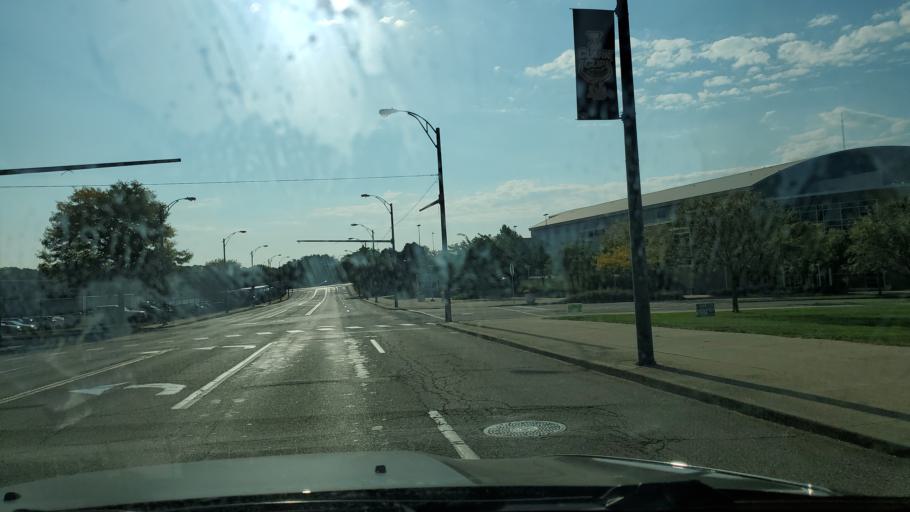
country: US
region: Ohio
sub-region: Mahoning County
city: Youngstown
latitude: 41.0976
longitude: -80.6490
